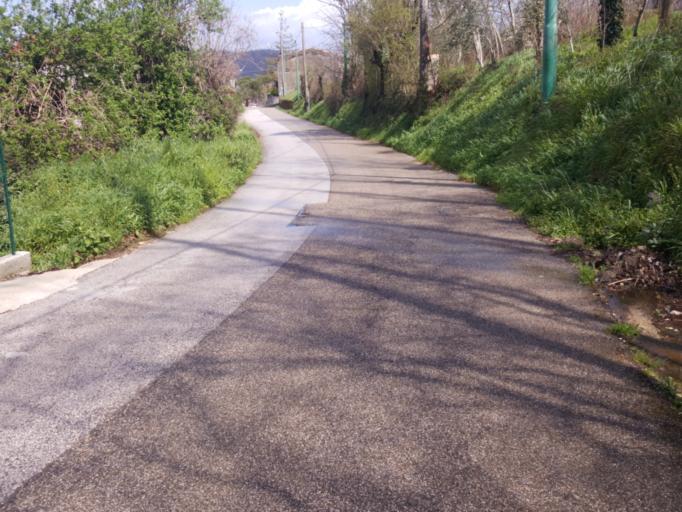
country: IT
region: Campania
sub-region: Provincia di Avellino
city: Roccabascerana
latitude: 41.0412
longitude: 14.7172
